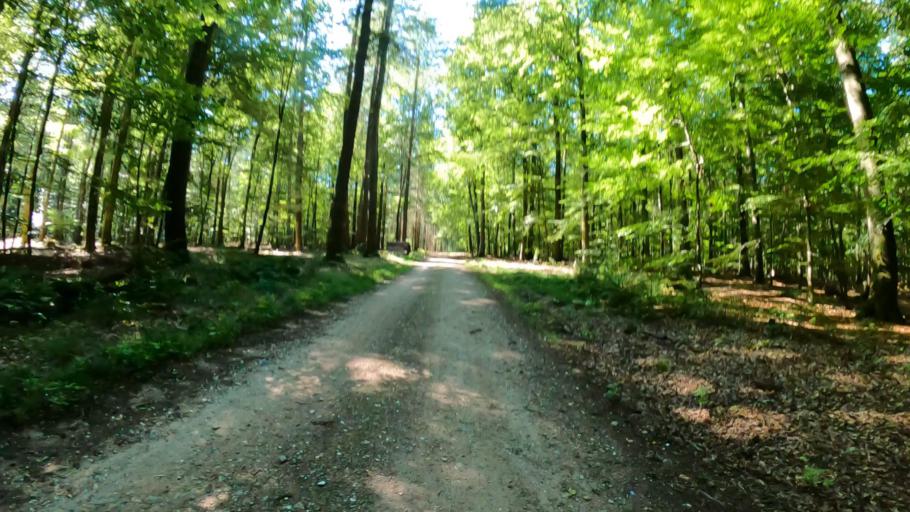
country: DE
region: Schleswig-Holstein
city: Kroppelshagen-Fahrendorf
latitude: 53.5047
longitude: 10.3393
